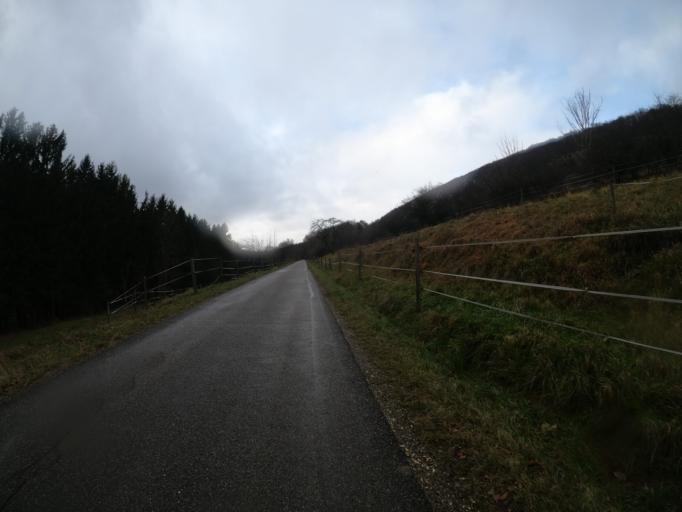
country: DE
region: Baden-Wuerttemberg
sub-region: Regierungsbezirk Stuttgart
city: Donzdorf
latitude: 48.7210
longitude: 9.8513
